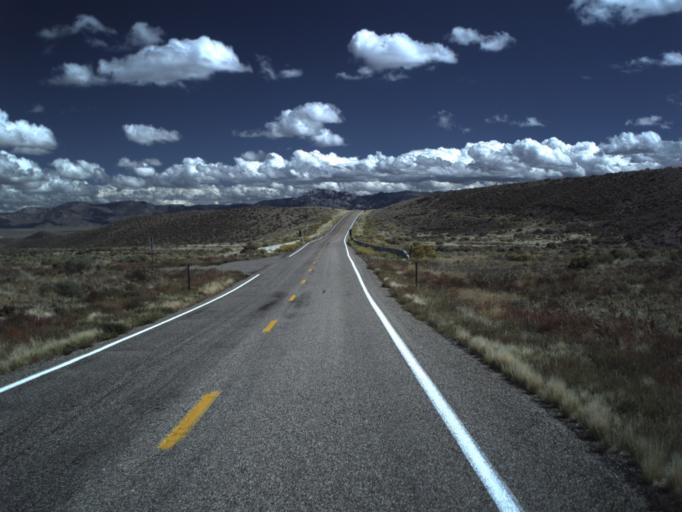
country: US
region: Utah
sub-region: Beaver County
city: Milford
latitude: 38.4392
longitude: -113.1543
